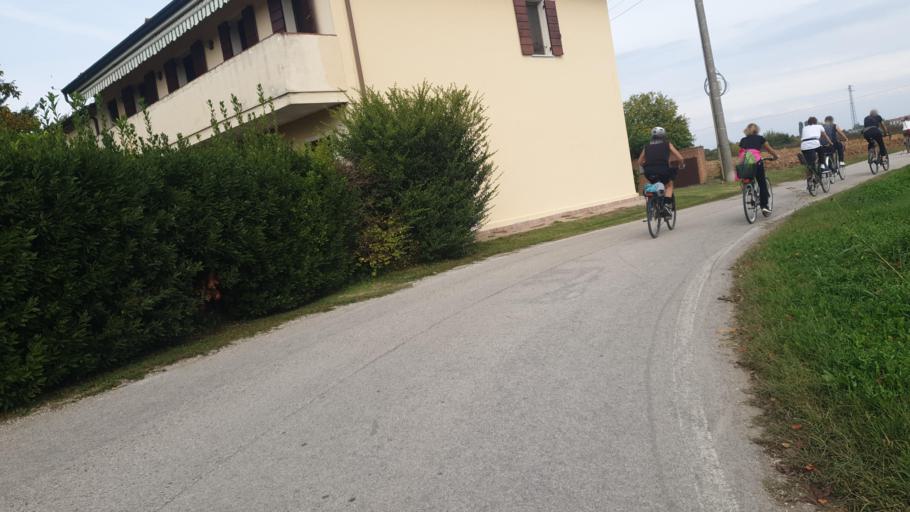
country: IT
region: Veneto
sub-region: Provincia di Padova
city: Cervarese Santa Croce
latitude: 45.4154
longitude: 11.7000
